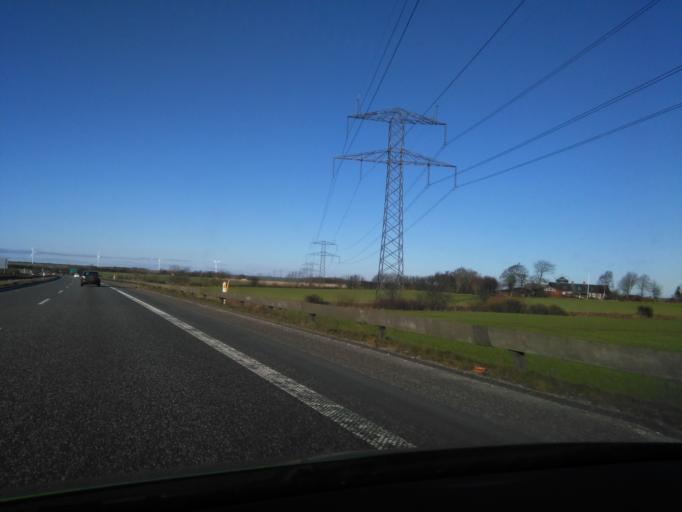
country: DK
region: Central Jutland
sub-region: Randers Kommune
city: Spentrup
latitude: 56.5038
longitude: 9.9757
